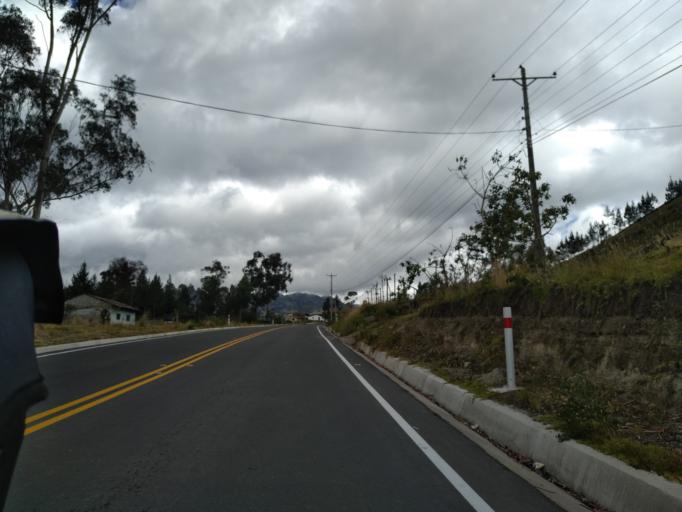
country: EC
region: Cotopaxi
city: Saquisili
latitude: -0.7922
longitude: -78.9127
